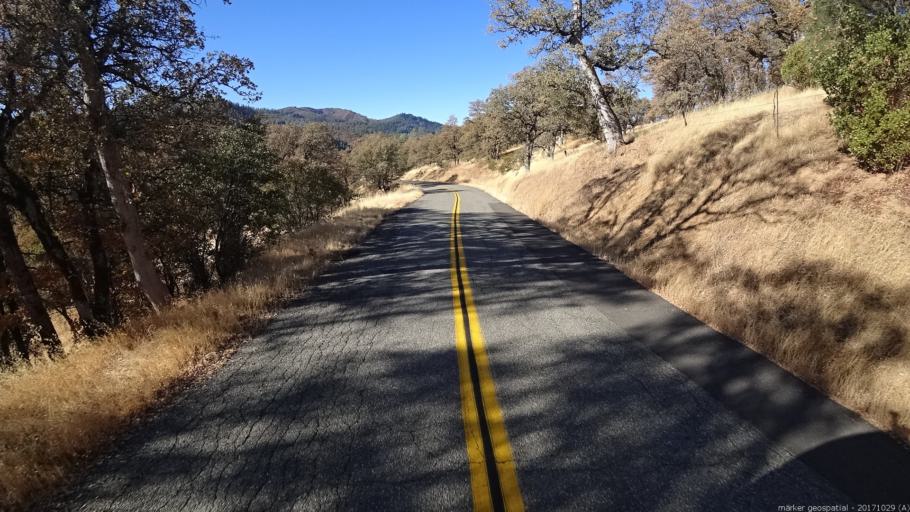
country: US
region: California
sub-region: Trinity County
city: Lewiston
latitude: 40.3631
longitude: -122.8845
